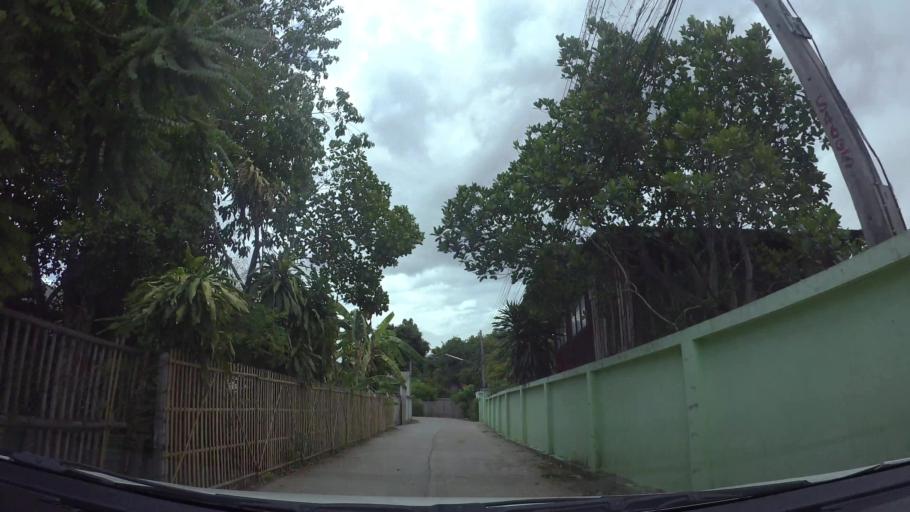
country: TH
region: Chiang Mai
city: Saraphi
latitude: 18.7449
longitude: 99.0446
